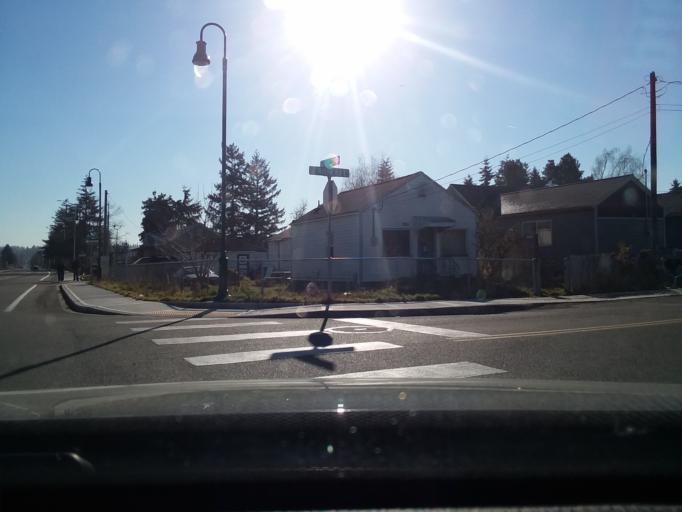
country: US
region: Washington
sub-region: Pierce County
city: Fife
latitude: 47.2463
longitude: -122.3648
